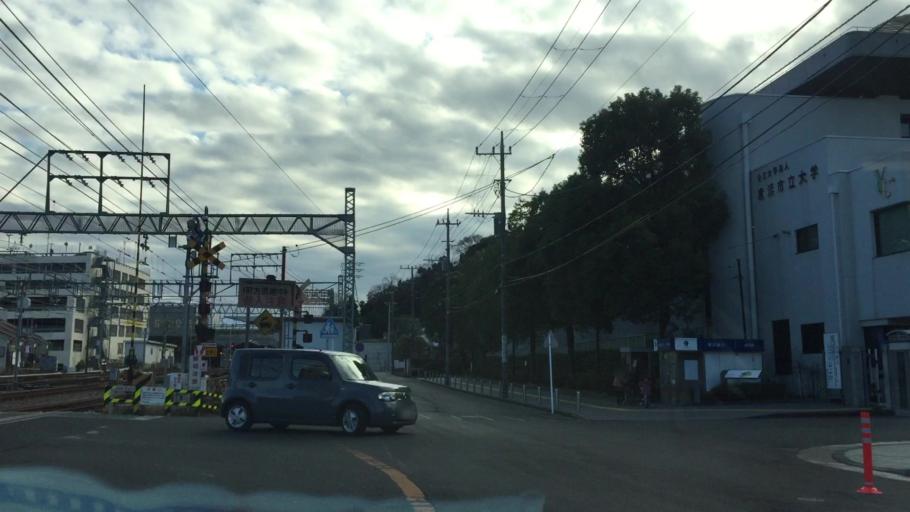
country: JP
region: Kanagawa
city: Zushi
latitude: 35.3338
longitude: 139.6199
